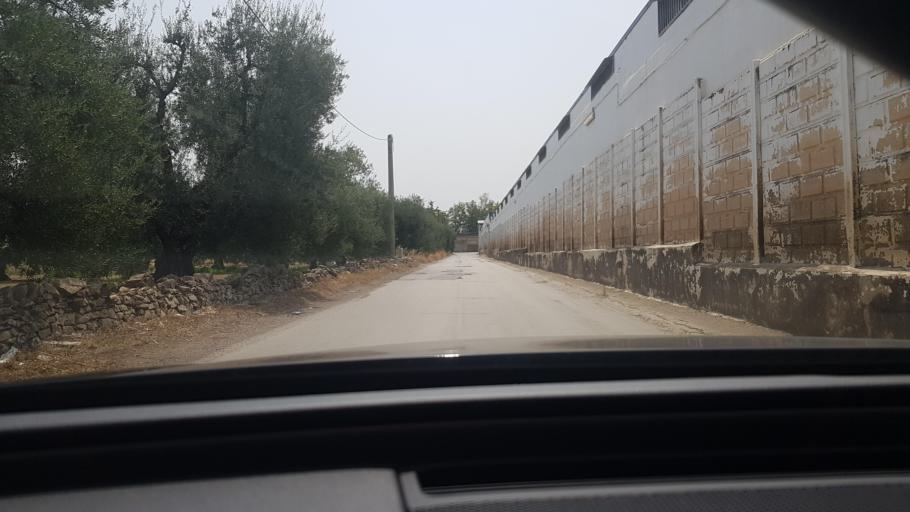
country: IT
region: Apulia
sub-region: Provincia di Barletta - Andria - Trani
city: Andria
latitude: 41.2166
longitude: 16.2606
